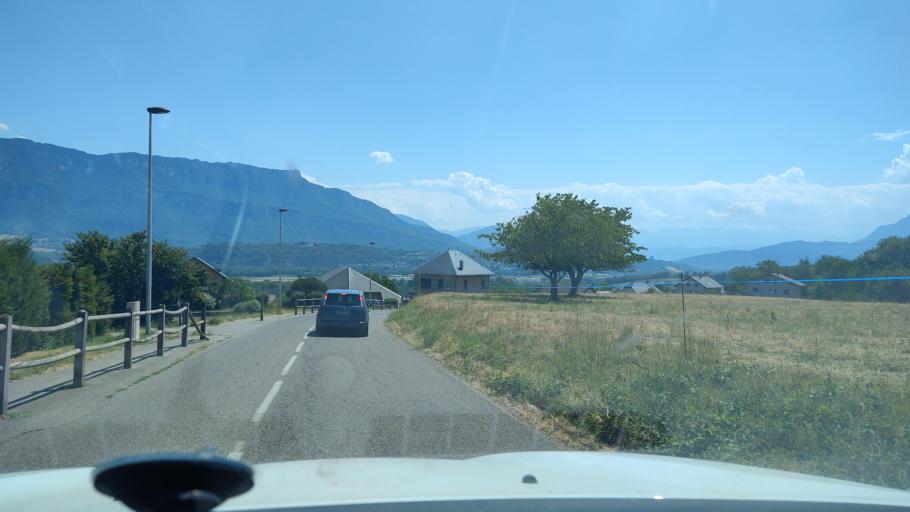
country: FR
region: Rhone-Alpes
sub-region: Departement de la Savoie
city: Le Bourget-du-Lac
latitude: 45.6533
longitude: 5.8518
